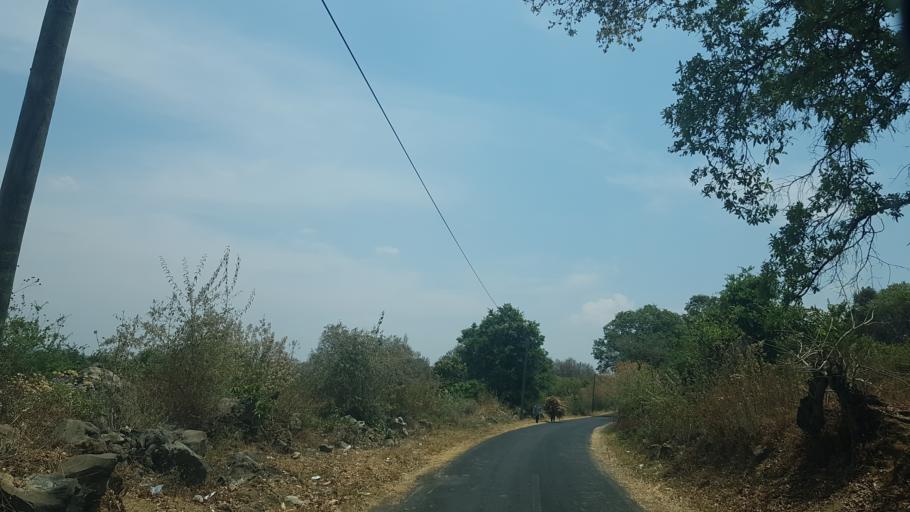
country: MX
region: Puebla
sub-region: Tochimilco
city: La Magdalena Yancuitlalpan
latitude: 18.8870
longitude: -98.6005
